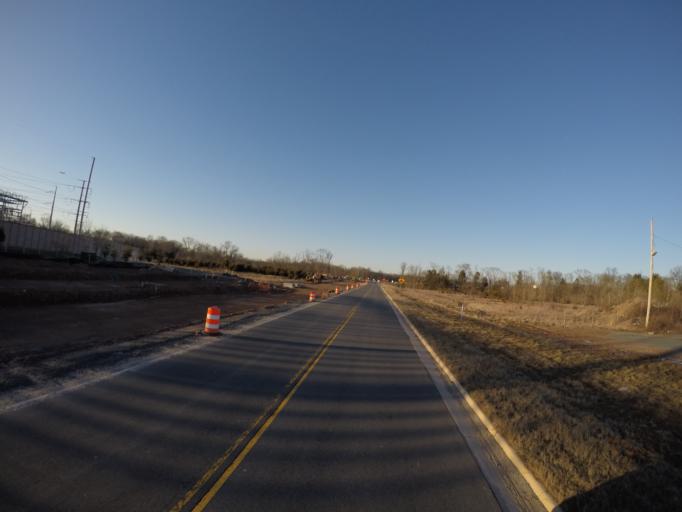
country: US
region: Virginia
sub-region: Loudoun County
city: Sterling
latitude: 39.0245
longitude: -77.4364
